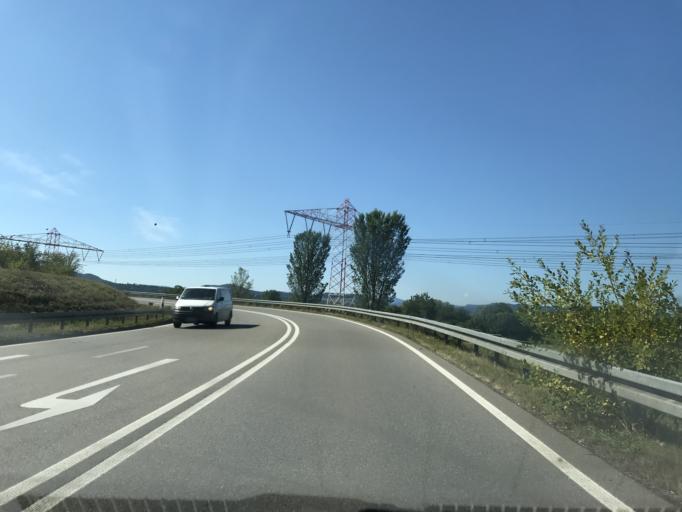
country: DE
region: Baden-Wuerttemberg
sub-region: Freiburg Region
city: Rheinfelden (Baden)
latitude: 47.5684
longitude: 7.7587
